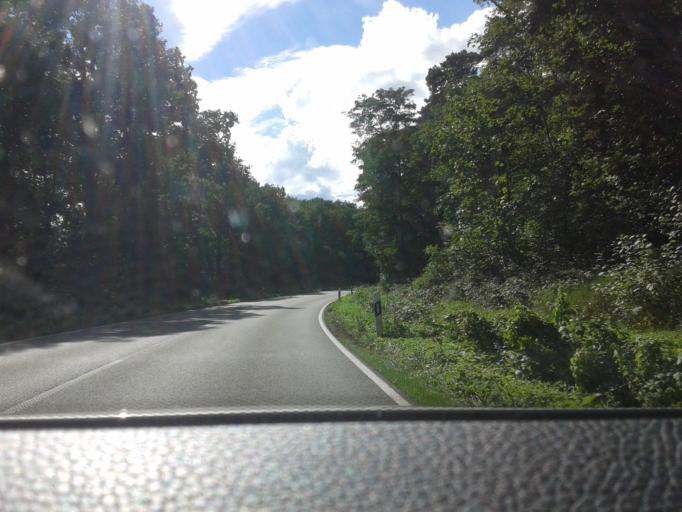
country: DE
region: North Rhine-Westphalia
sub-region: Regierungsbezirk Dusseldorf
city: Weeze
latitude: 51.6158
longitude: 6.2321
